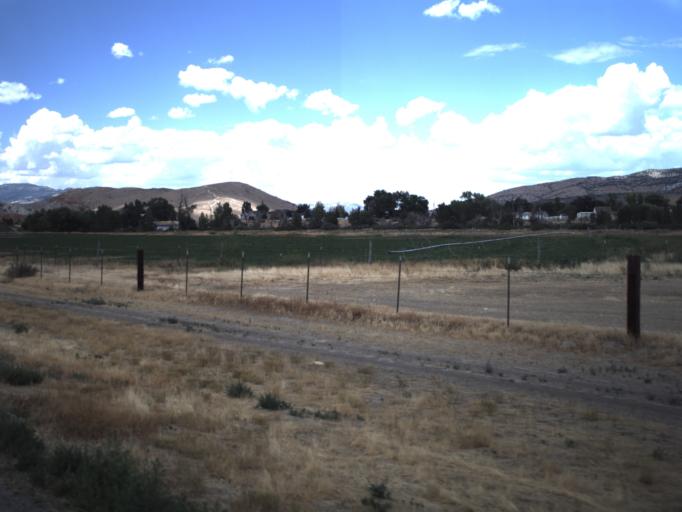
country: US
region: Utah
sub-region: Sanpete County
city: Centerfield
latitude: 39.1206
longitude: -111.7140
